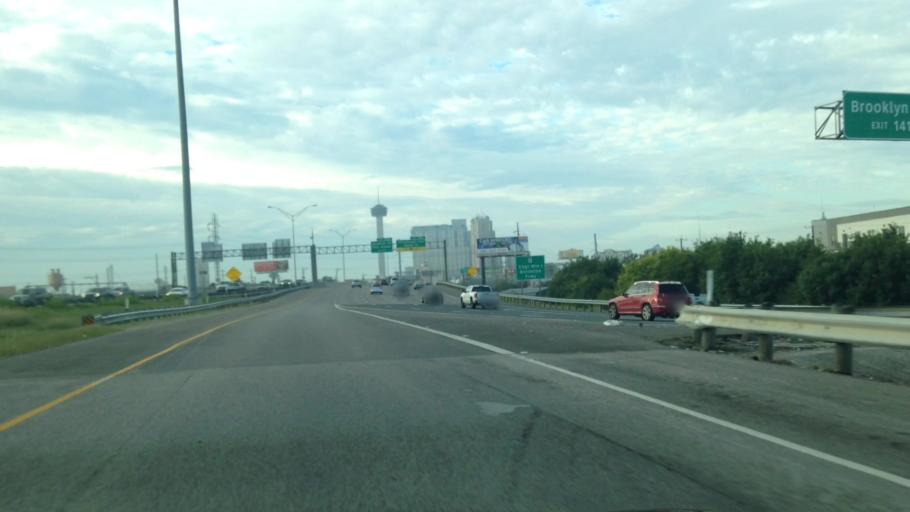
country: US
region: Texas
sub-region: Bexar County
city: San Antonio
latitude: 29.4363
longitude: -98.4775
